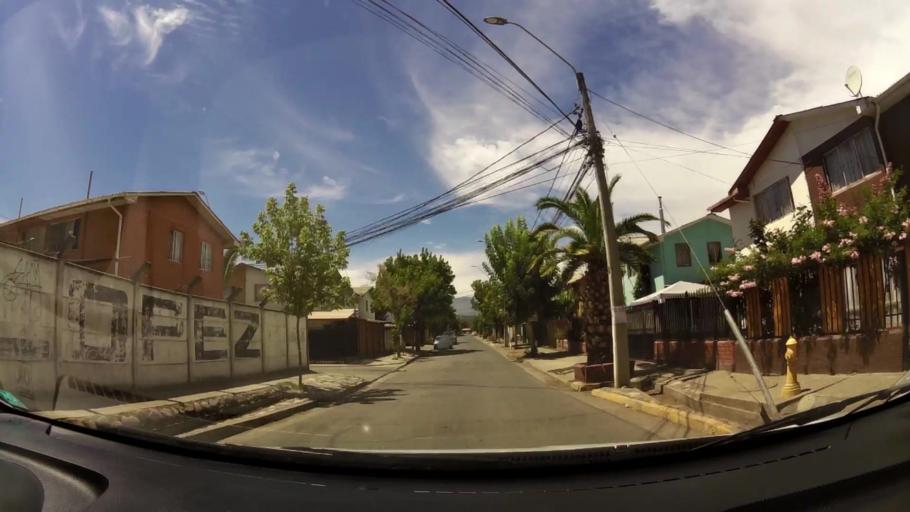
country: CL
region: O'Higgins
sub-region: Provincia de Cachapoal
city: Graneros
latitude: -34.0602
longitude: -70.7289
